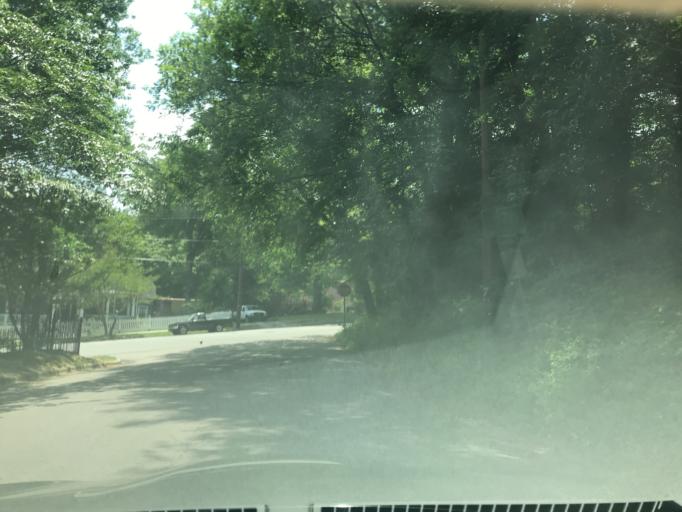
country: US
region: North Carolina
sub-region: Wake County
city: Raleigh
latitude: 35.7851
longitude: -78.6294
